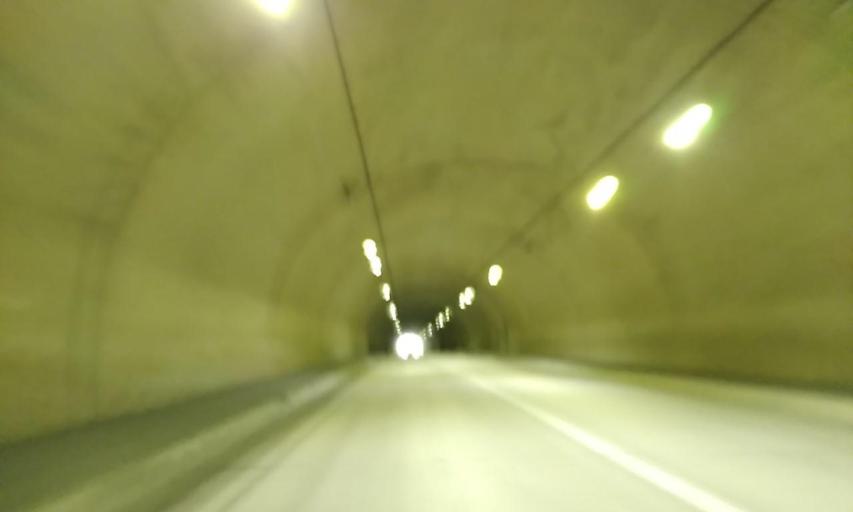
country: JP
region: Mie
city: Toba
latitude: 34.5012
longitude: 136.7811
